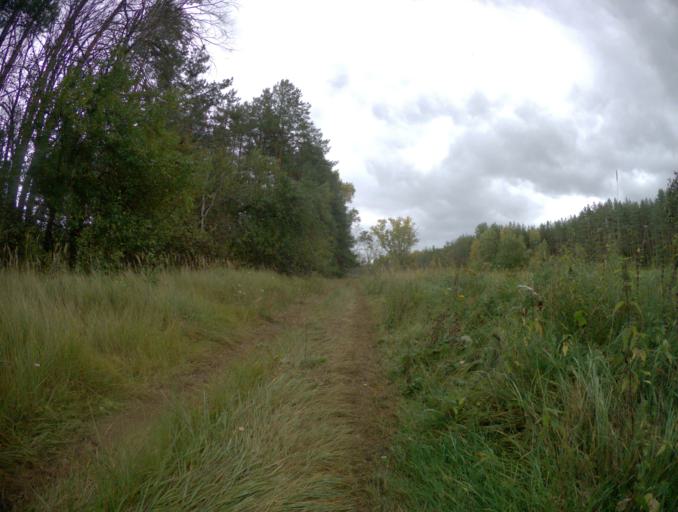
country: RU
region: Moskovskaya
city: Misheronskiy
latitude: 55.7752
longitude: 39.6109
